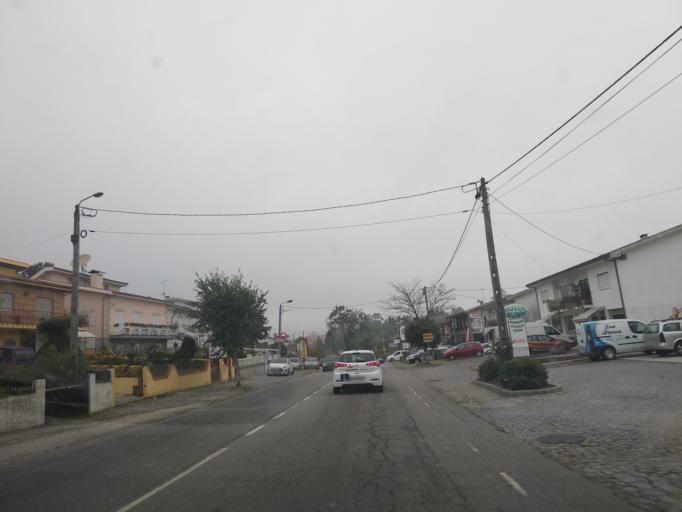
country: PT
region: Braga
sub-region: Vila Verde
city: Vila Verde
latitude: 41.6366
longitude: -8.4337
